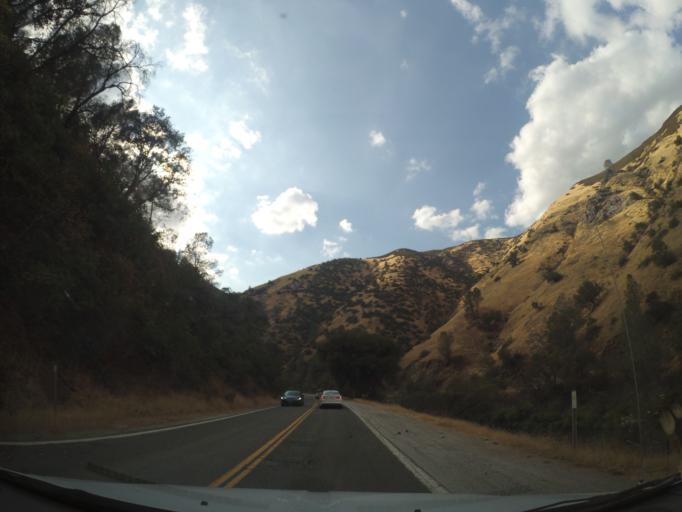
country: US
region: California
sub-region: Mariposa County
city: Midpines
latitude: 37.6314
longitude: -119.9425
